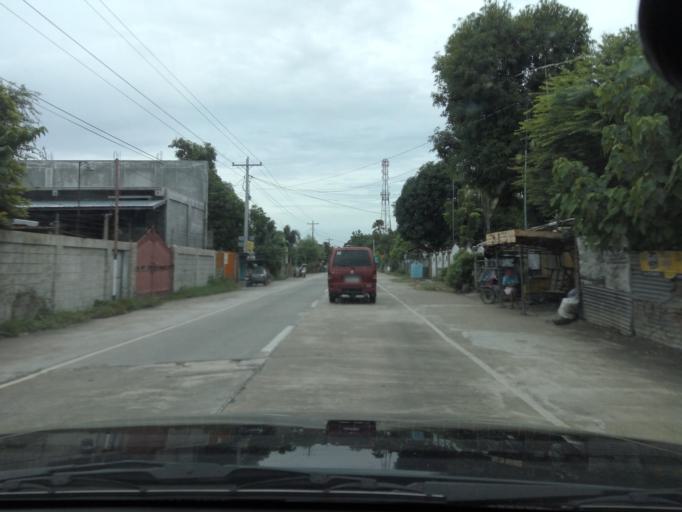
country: PH
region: Central Luzon
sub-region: Province of Nueva Ecija
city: Rajal Norte
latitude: 15.4425
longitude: 120.8484
